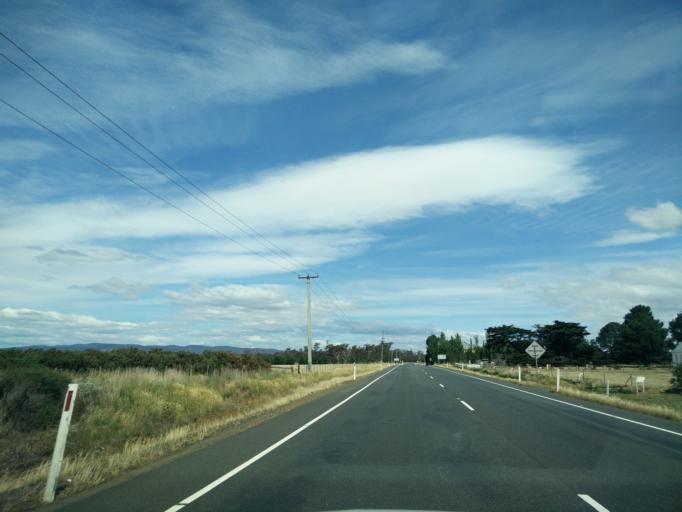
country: AU
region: Tasmania
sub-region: Northern Midlands
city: Evandale
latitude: -41.8049
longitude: 147.4044
